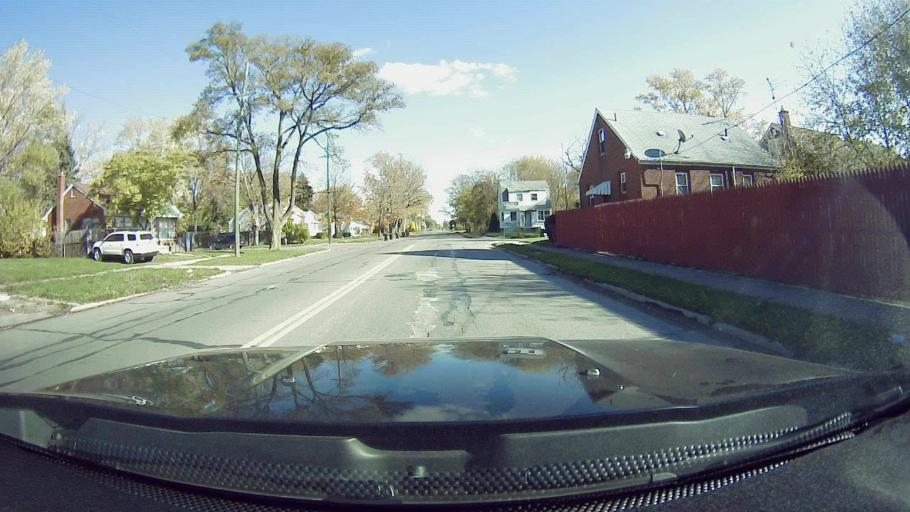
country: US
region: Michigan
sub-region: Wayne County
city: Dearborn Heights
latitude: 42.3516
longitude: -83.2233
